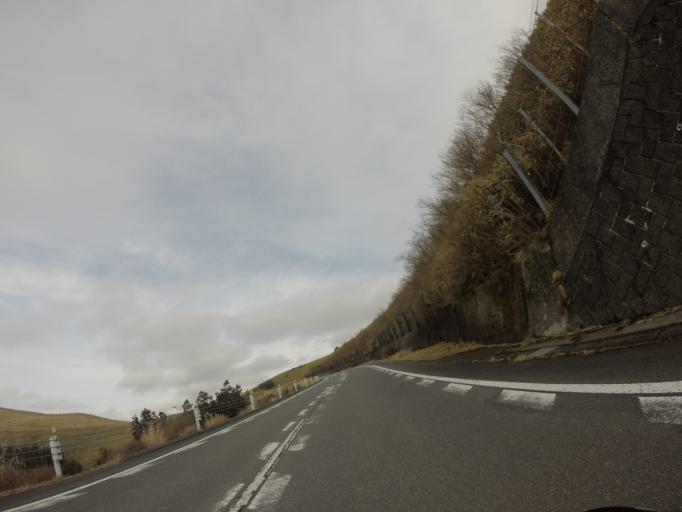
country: JP
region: Shizuoka
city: Heda
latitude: 34.8611
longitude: 138.8435
